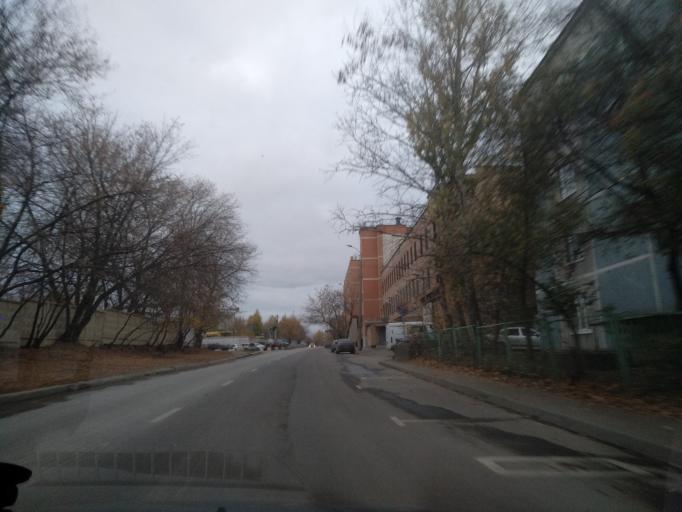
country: RU
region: Moscow
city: Kozeyevo
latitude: 55.8813
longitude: 37.6291
